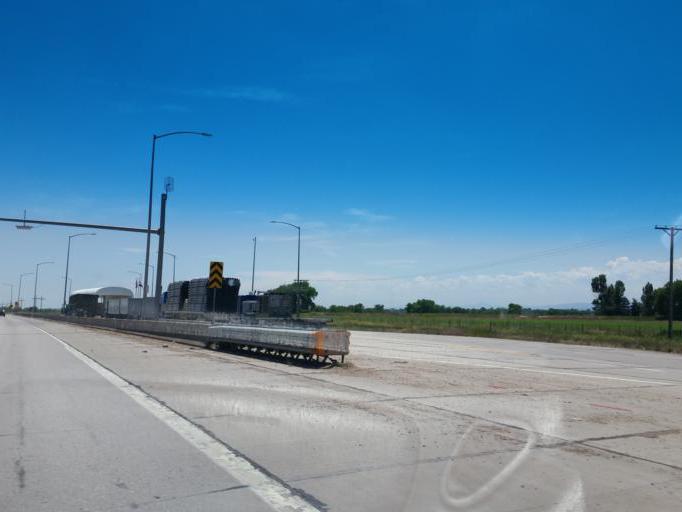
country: US
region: Colorado
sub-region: Larimer County
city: Fort Collins
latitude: 40.5576
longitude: -105.0012
